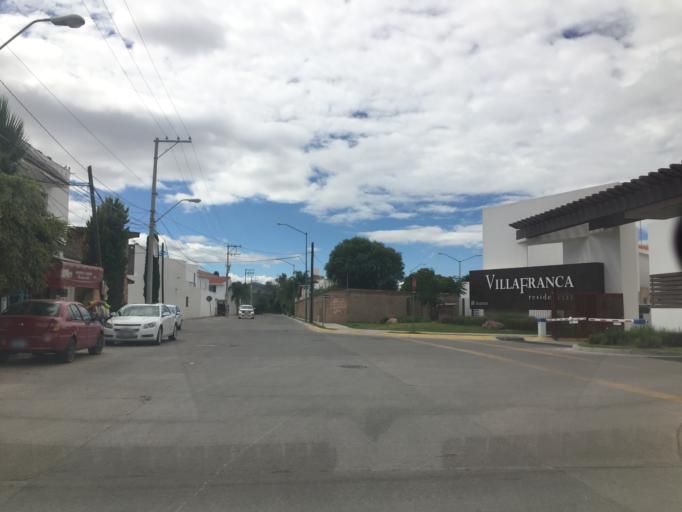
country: MX
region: Guanajuato
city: Leon
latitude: 21.1539
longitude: -101.6594
